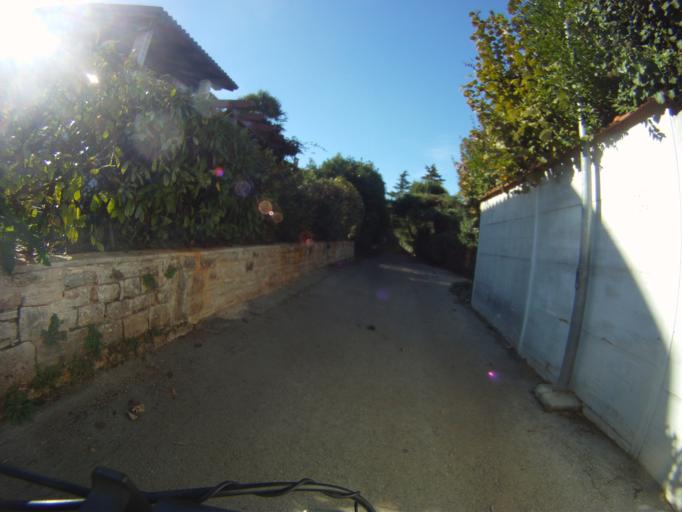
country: HR
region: Istarska
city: Novigrad
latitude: 45.3522
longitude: 13.5468
